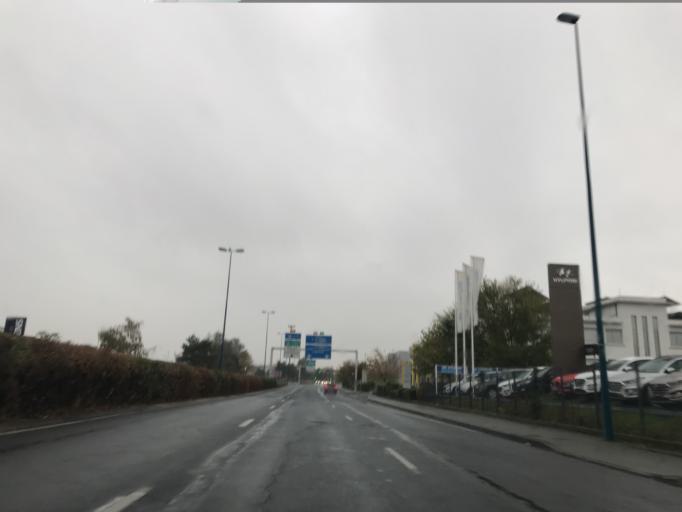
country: FR
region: Auvergne
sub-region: Departement du Puy-de-Dome
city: Aubiere
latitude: 45.7793
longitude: 3.1222
